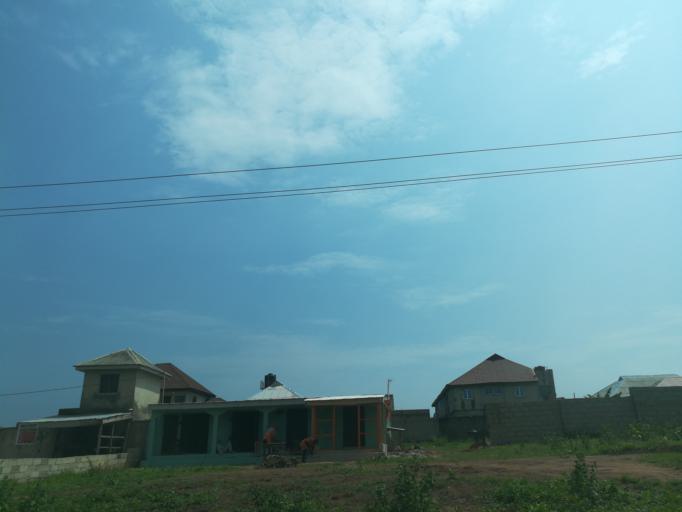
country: NG
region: Lagos
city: Ikorodu
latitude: 6.5956
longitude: 3.6339
